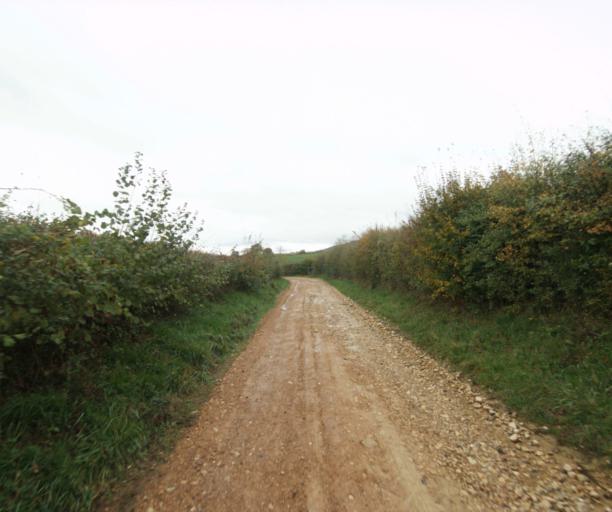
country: FR
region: Bourgogne
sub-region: Departement de Saone-et-Loire
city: Tournus
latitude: 46.4853
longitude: 4.8635
